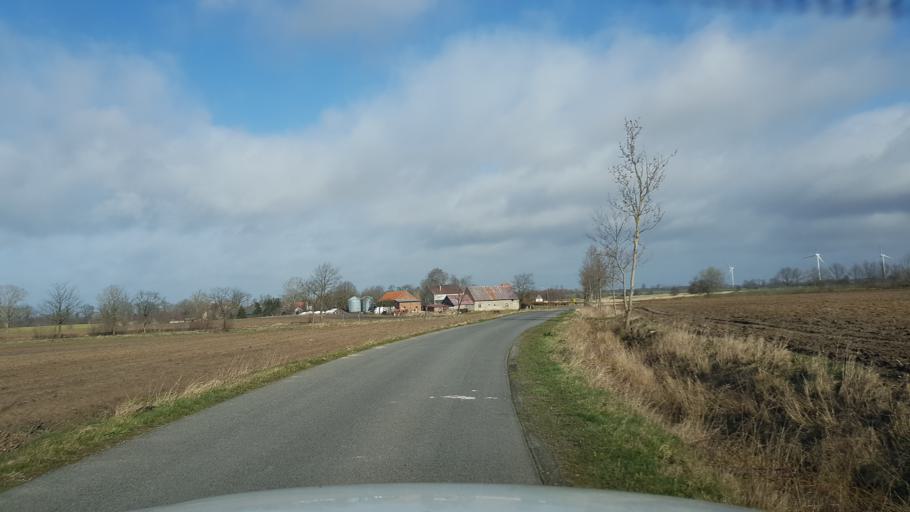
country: PL
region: West Pomeranian Voivodeship
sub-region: Powiat slawienski
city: Slawno
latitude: 54.5075
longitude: 16.6529
